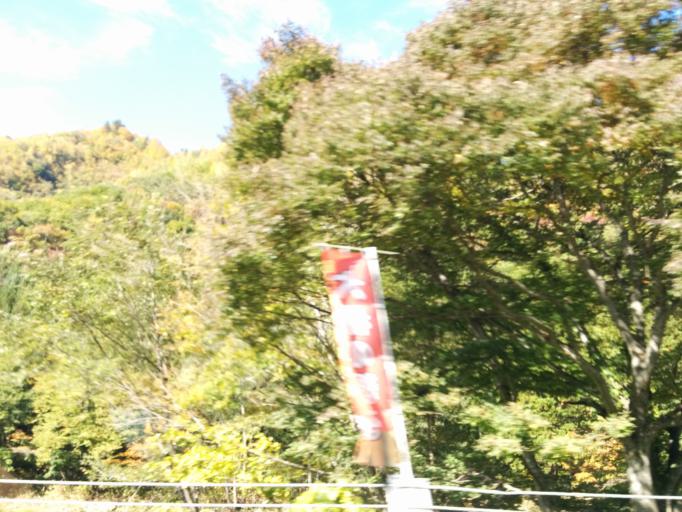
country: JP
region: Tochigi
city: Nikko
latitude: 37.1127
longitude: 139.4545
